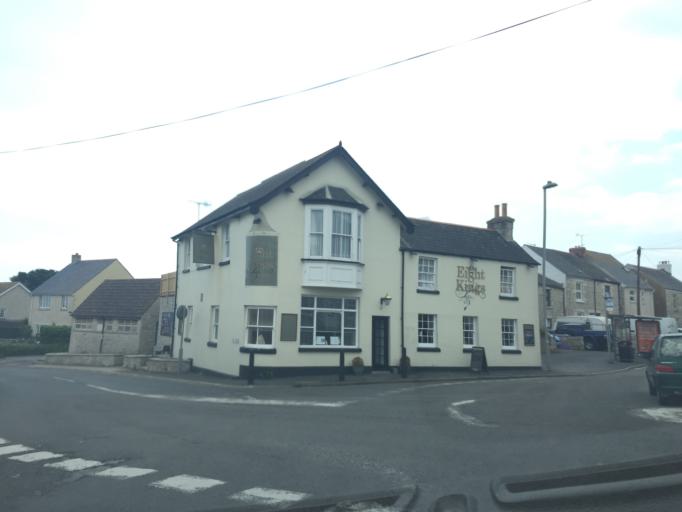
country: GB
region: England
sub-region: Dorset
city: Easton
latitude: 50.5295
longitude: -2.4410
